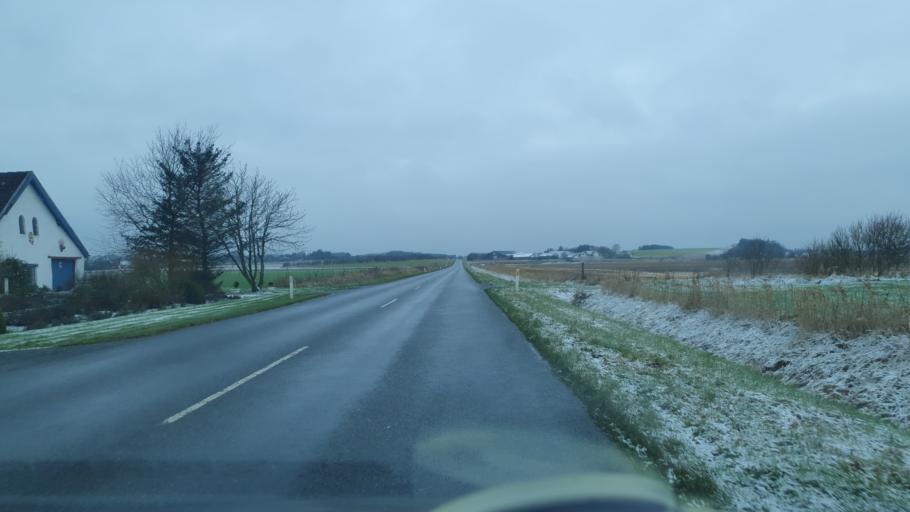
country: DK
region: North Denmark
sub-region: Jammerbugt Kommune
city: Brovst
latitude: 57.1183
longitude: 9.4976
